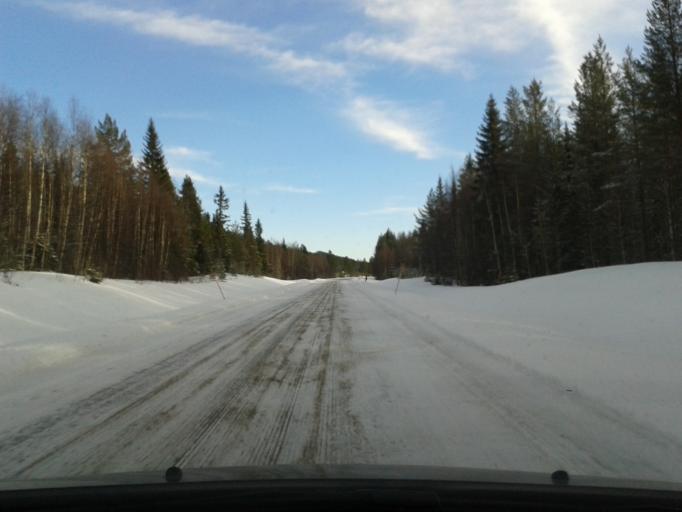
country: SE
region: Vaesterbotten
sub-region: Asele Kommun
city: Asele
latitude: 64.3125
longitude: 17.2273
